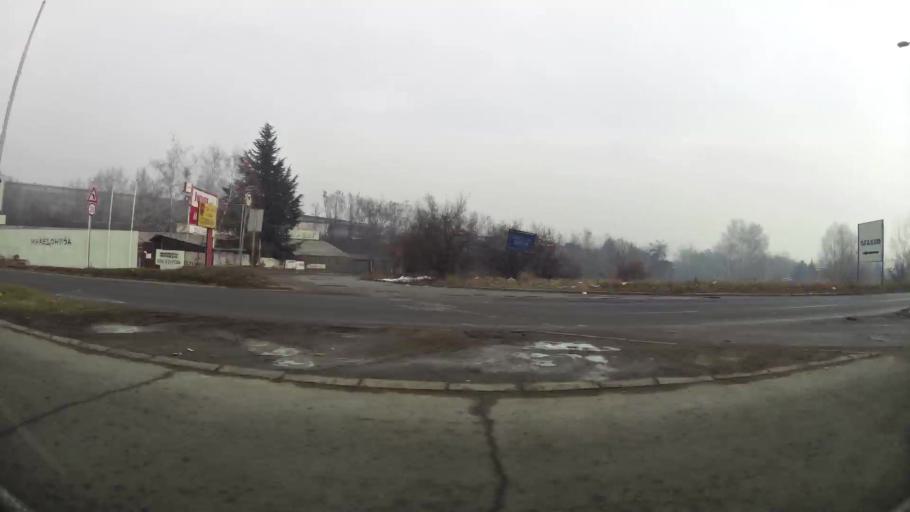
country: MK
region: Cair
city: Cair
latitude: 42.0039
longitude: 21.4702
